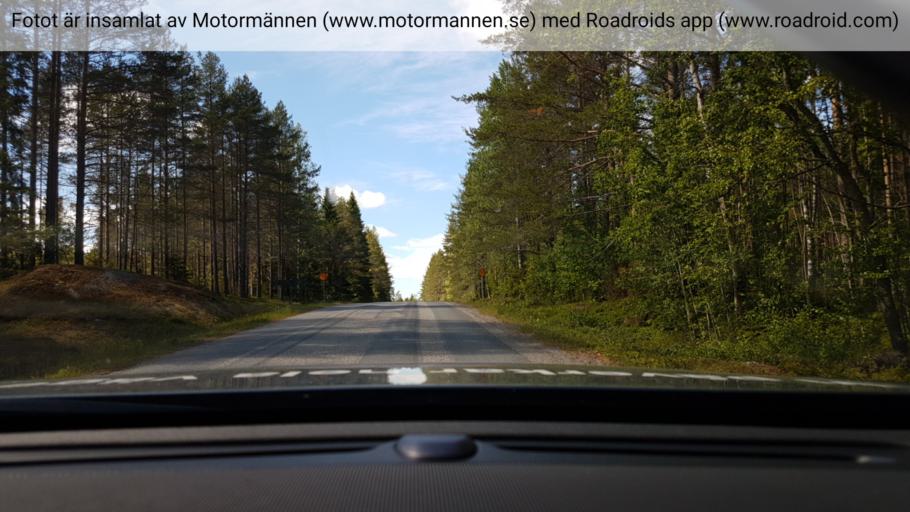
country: SE
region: Vaesterbotten
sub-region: Skelleftea Kommun
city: Burea
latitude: 64.4642
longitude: 21.3850
